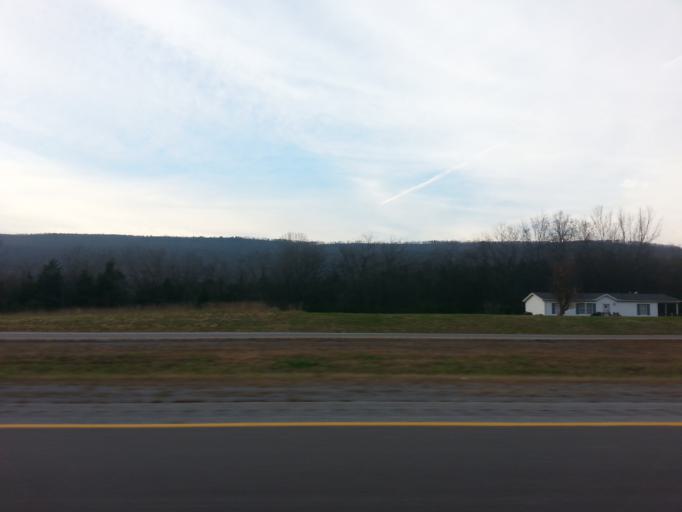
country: US
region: Tennessee
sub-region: Rhea County
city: Spring City
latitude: 35.6388
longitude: -84.8958
